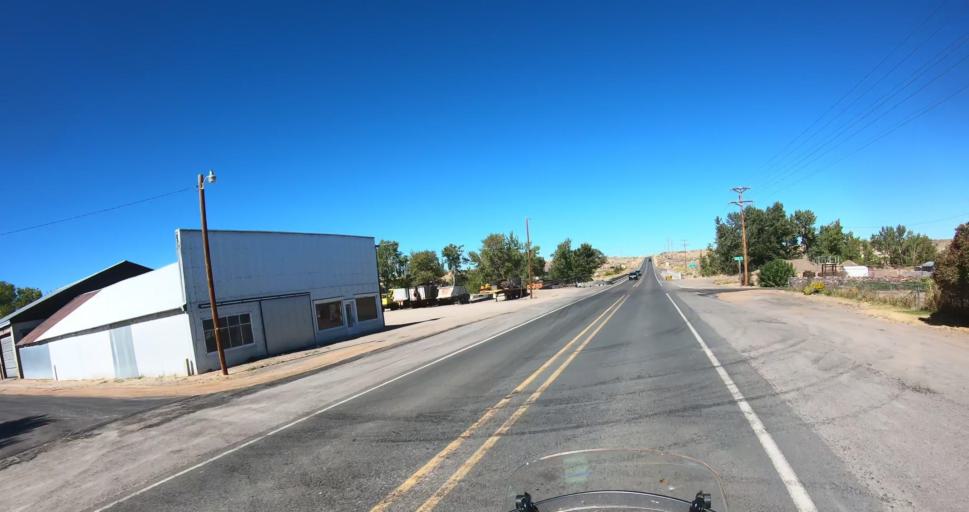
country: US
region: Oregon
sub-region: Lake County
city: Lakeview
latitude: 42.6943
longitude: -120.5456
